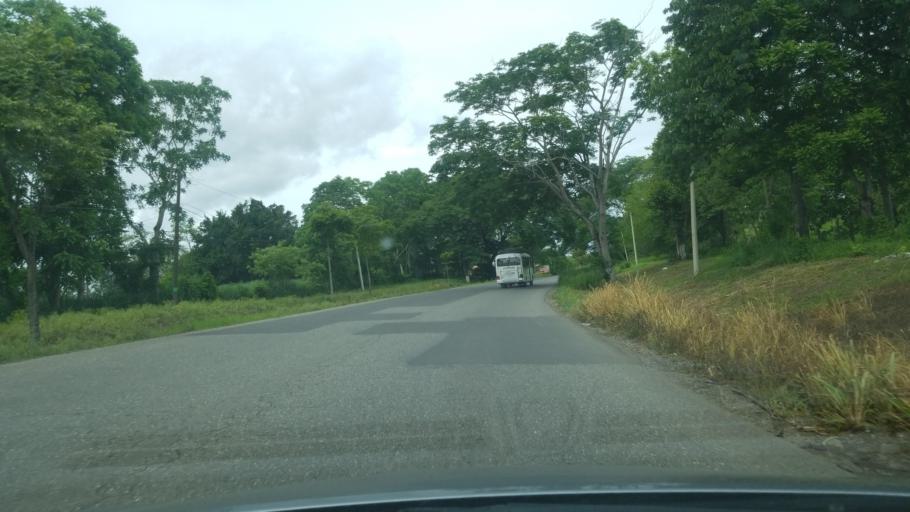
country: HN
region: Santa Barbara
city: San Marcos
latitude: 15.3054
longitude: -88.4426
